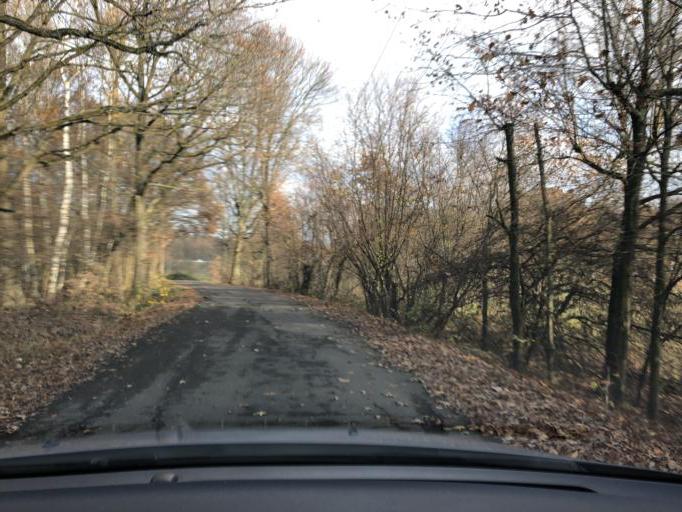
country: DE
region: Saxony
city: Grimma
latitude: 51.2553
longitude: 12.7438
